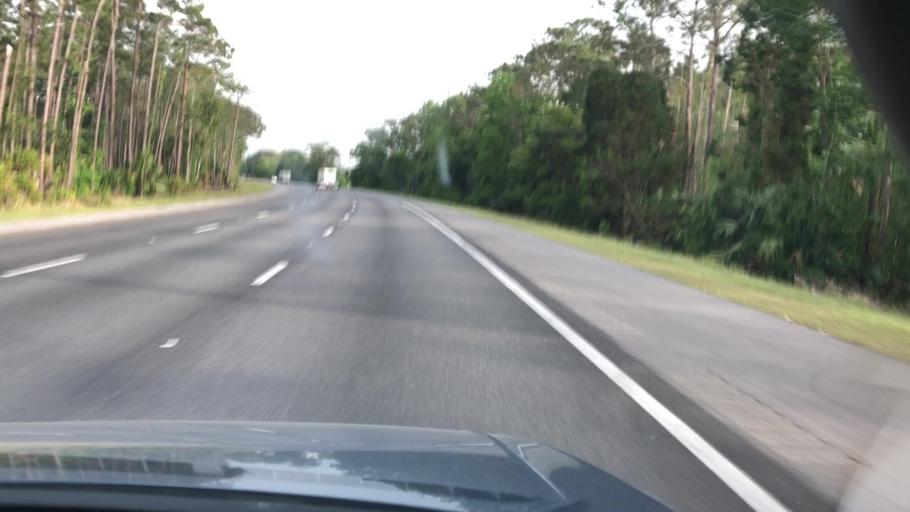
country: US
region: Florida
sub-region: Volusia County
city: Port Orange
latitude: 29.1303
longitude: -81.0610
